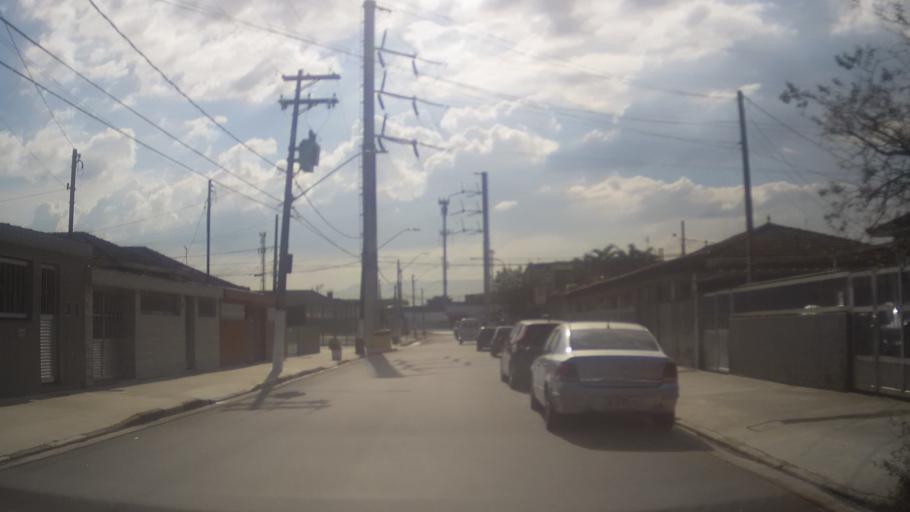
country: BR
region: Sao Paulo
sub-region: Santos
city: Santos
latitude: -23.9324
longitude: -46.3554
